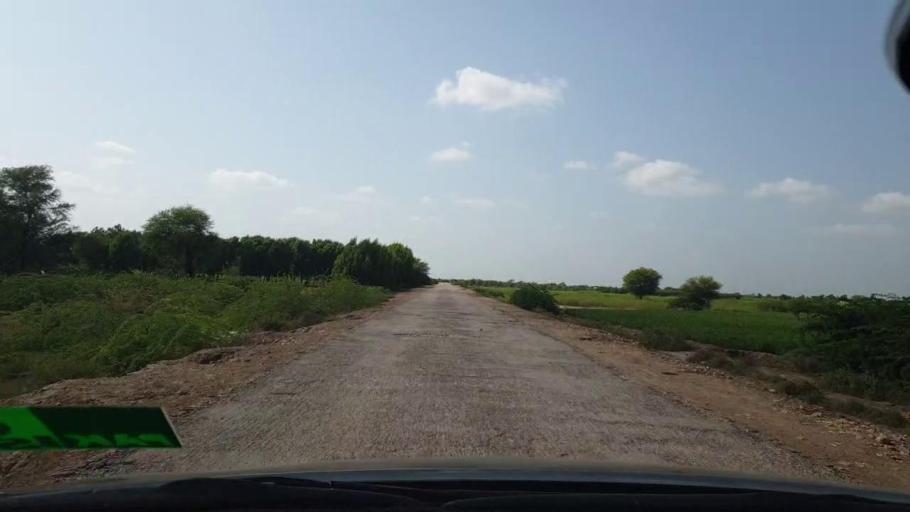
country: PK
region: Sindh
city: Tando Bago
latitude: 24.6626
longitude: 69.2022
